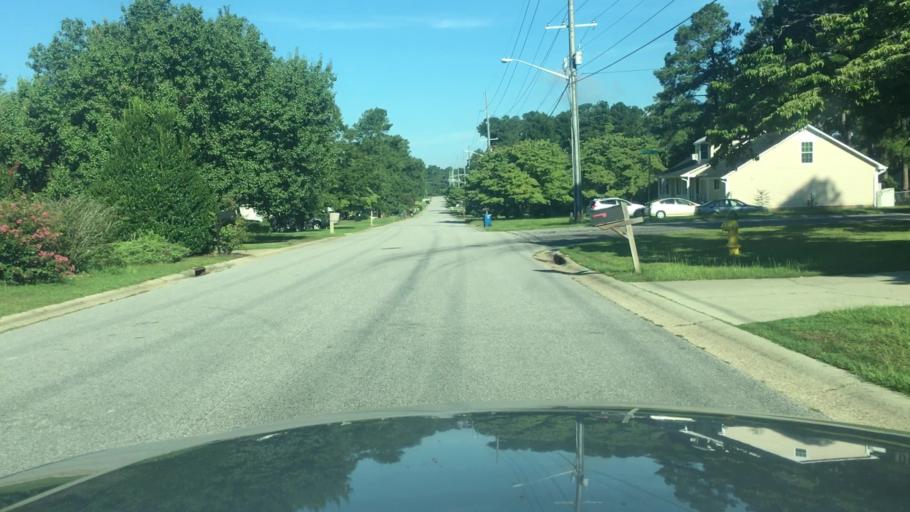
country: US
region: North Carolina
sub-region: Cumberland County
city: Fayetteville
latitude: 35.1296
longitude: -78.8851
